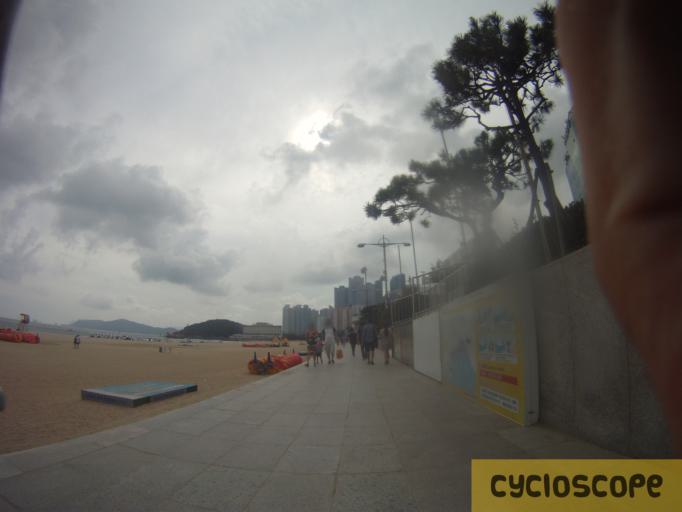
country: KR
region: Busan
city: Kijang
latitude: 35.1591
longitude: 129.1607
